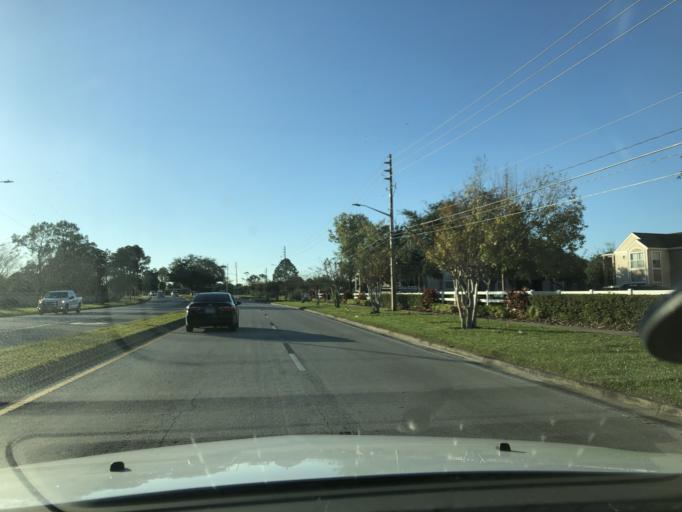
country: US
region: Florida
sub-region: Orange County
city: Oak Ridge
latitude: 28.4973
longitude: -81.4435
